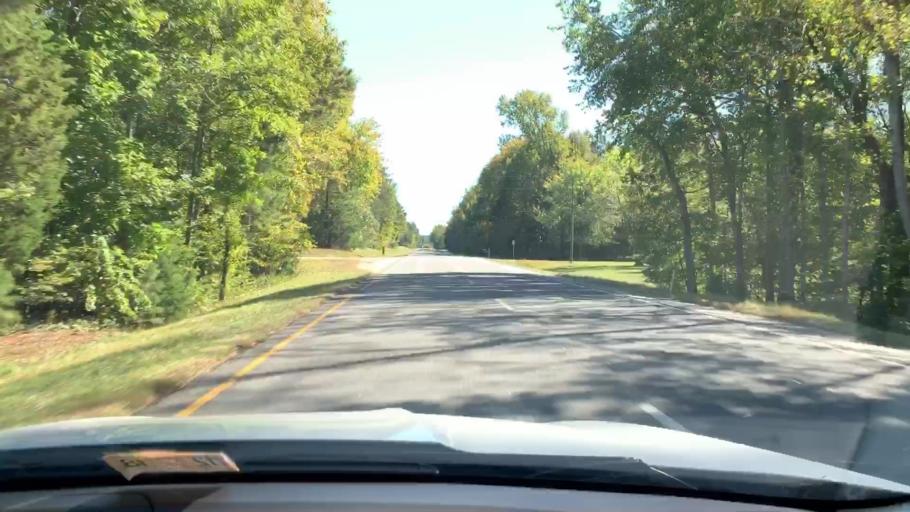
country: US
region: Virginia
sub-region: King and Queen County
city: King and Queen Court House
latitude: 37.7639
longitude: -76.7316
